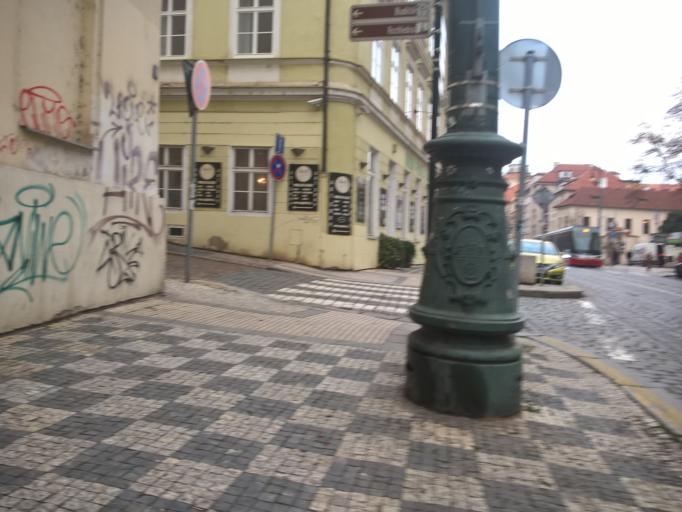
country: CZ
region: Praha
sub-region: Praha 1
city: Mala Strana
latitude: 50.0827
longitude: 14.4044
